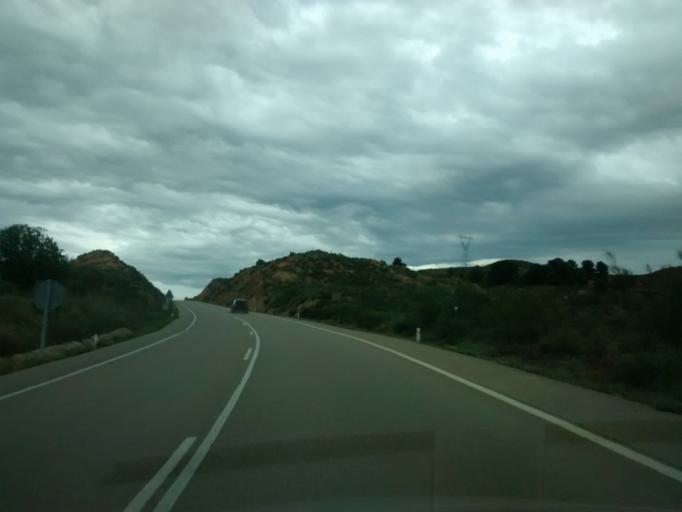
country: ES
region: Aragon
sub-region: Provincia de Zaragoza
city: Caspe
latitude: 41.1996
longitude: 0.0425
